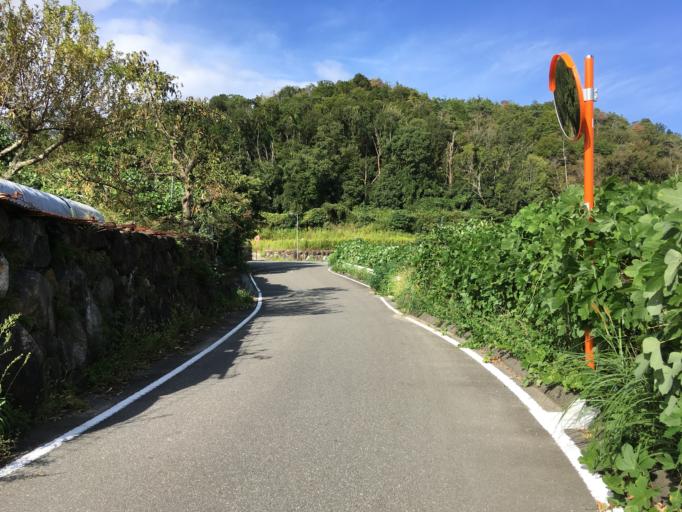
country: JP
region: Nara
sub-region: Ikoma-shi
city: Ikoma
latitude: 34.6715
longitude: 135.6963
